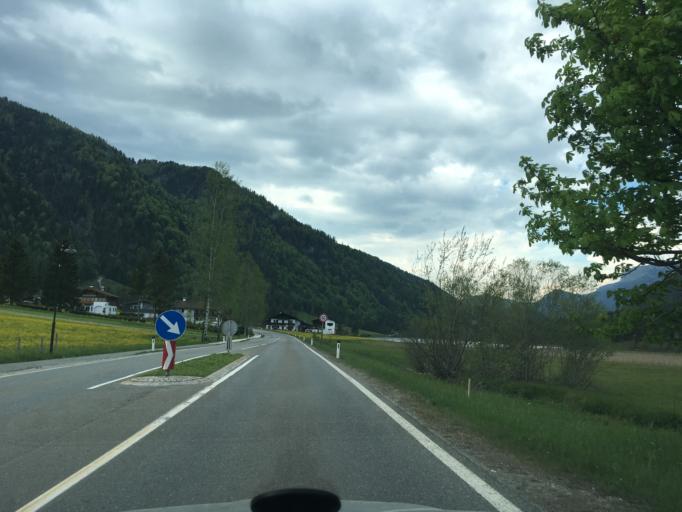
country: AT
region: Tyrol
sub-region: Politischer Bezirk Kitzbuhel
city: Fieberbrunn
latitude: 47.5303
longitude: 12.5728
